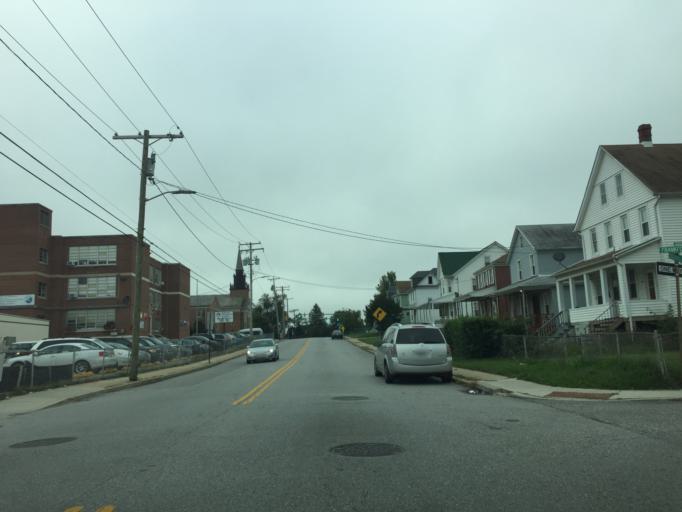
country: US
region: Maryland
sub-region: Baltimore County
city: Rosedale
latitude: 39.3363
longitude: -76.5499
